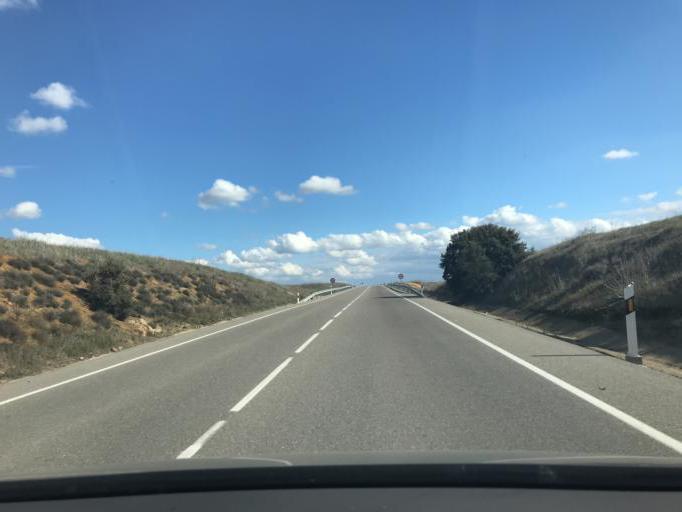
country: ES
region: Extremadura
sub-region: Provincia de Badajoz
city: Granja de Torrehermosa
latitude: 38.2917
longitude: -5.5363
